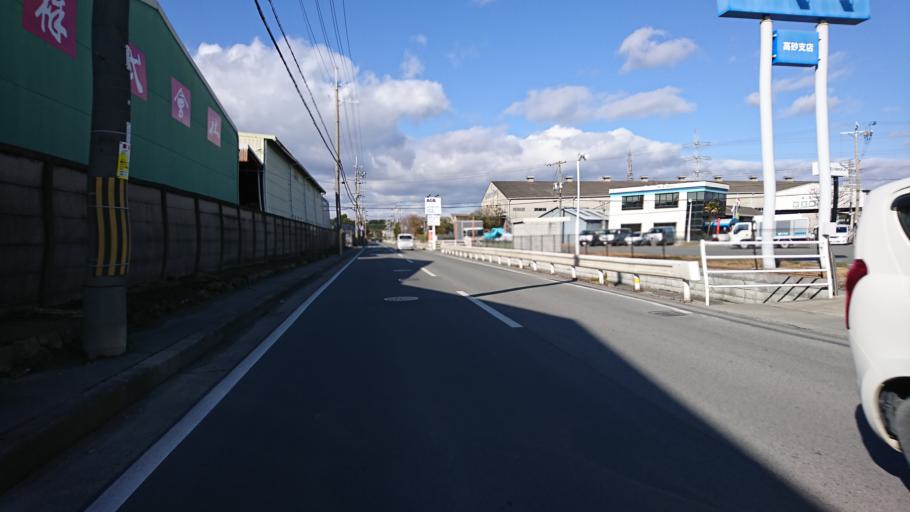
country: JP
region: Hyogo
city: Kakogawacho-honmachi
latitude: 34.7670
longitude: 134.7744
